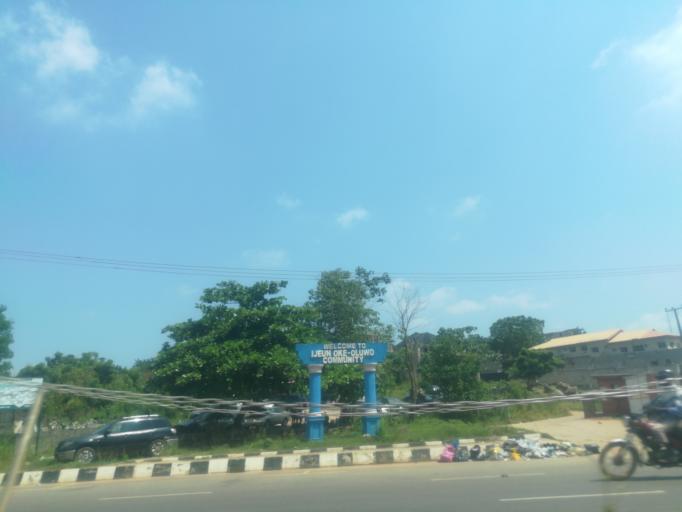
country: NG
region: Ogun
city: Abeokuta
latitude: 7.1411
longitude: 3.3642
